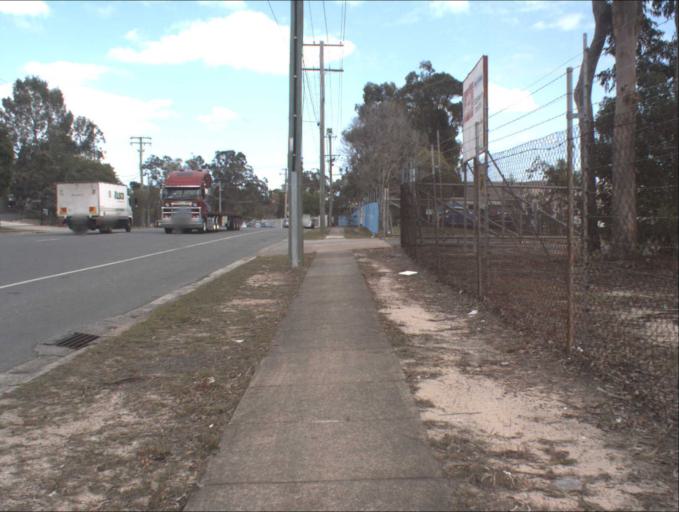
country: AU
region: Queensland
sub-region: Logan
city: Logan Reserve
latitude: -27.6778
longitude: 153.0739
